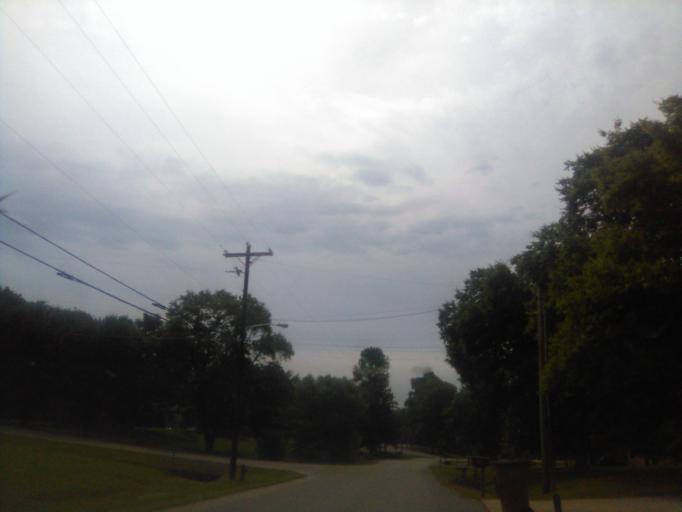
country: US
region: Tennessee
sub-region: Davidson County
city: Belle Meade
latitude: 36.0927
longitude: -86.8955
